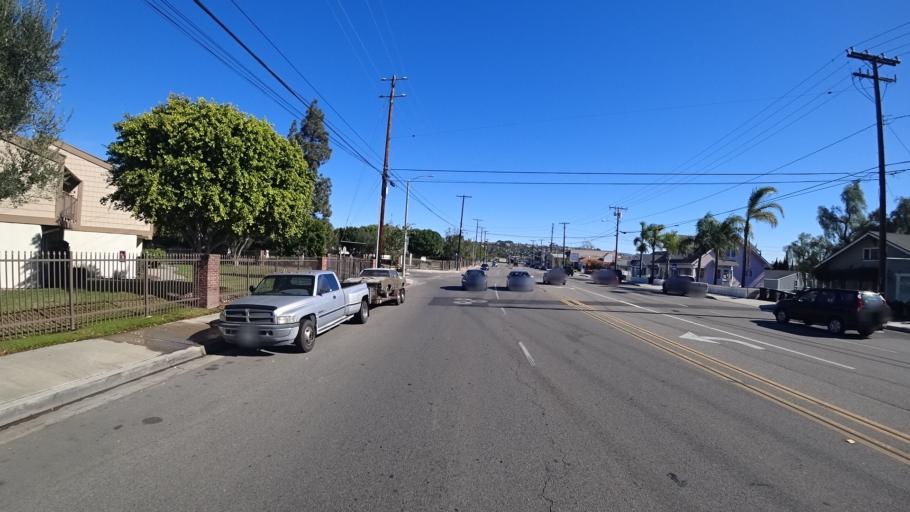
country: US
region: California
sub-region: Orange County
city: Villa Park
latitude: 33.8362
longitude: -117.8484
